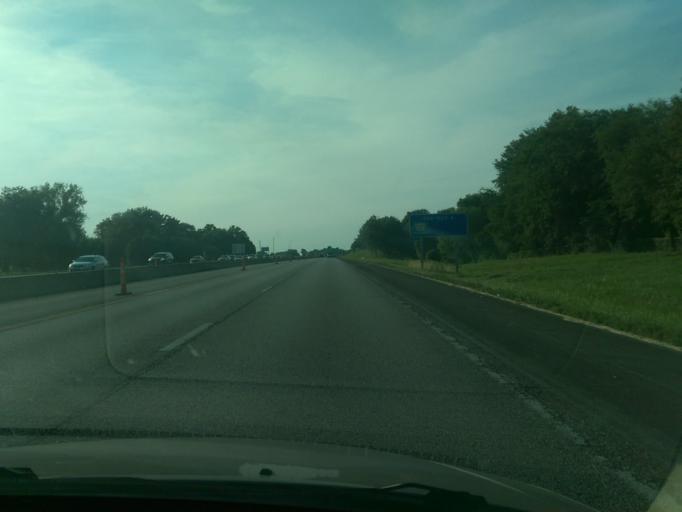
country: US
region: Missouri
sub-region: Platte County
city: Parkville
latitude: 39.2180
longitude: -94.6451
